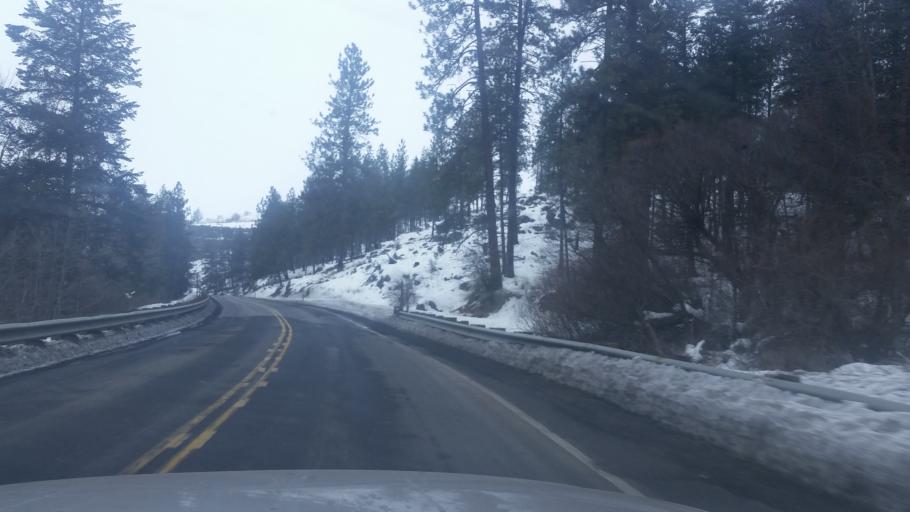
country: US
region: Washington
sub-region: Spokane County
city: Medical Lake
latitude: 47.7389
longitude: -117.8747
